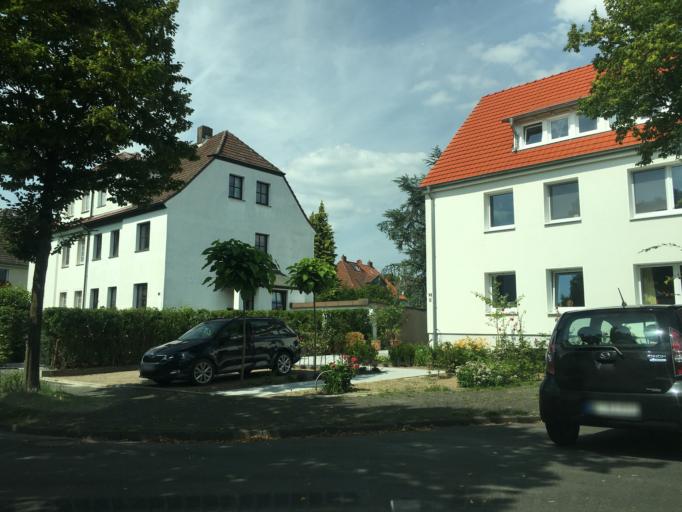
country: DE
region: North Rhine-Westphalia
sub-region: Regierungsbezirk Munster
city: Muenster
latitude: 51.9365
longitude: 7.6208
